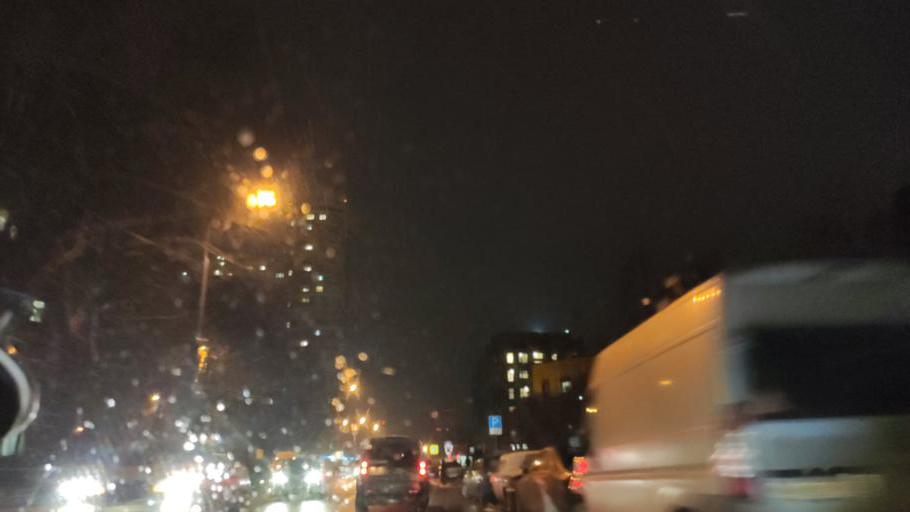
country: RU
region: Moskovskaya
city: Odintsovo
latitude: 55.6851
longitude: 37.2621
